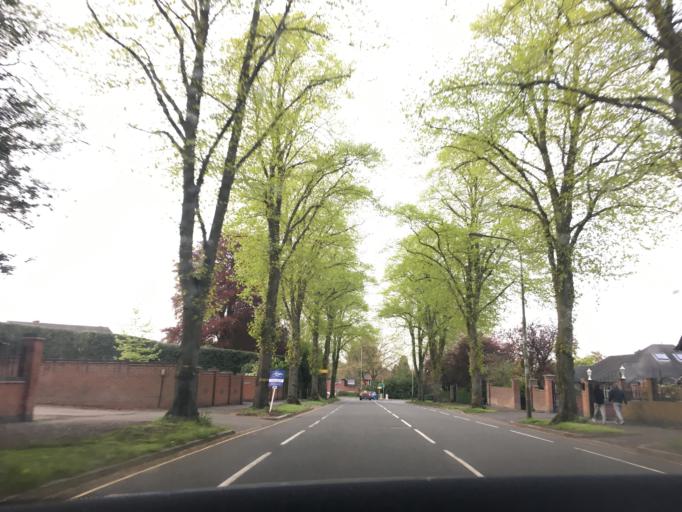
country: GB
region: England
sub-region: Leicestershire
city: Oadby
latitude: 52.6318
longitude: -1.0637
